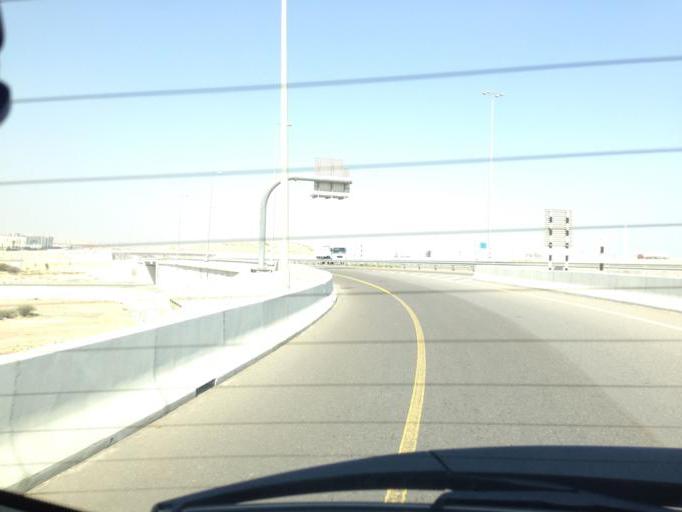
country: OM
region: Muhafazat Masqat
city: As Sib al Jadidah
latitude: 23.5660
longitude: 58.1915
